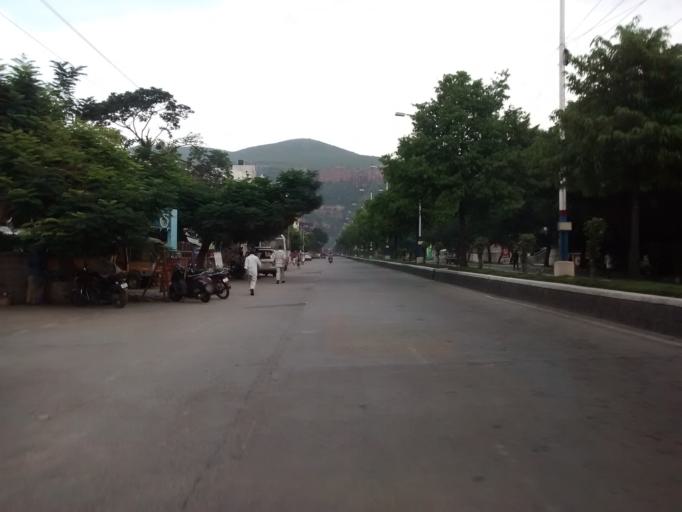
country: IN
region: Andhra Pradesh
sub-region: Chittoor
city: Akkarampalle
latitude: 13.6482
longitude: 79.4256
